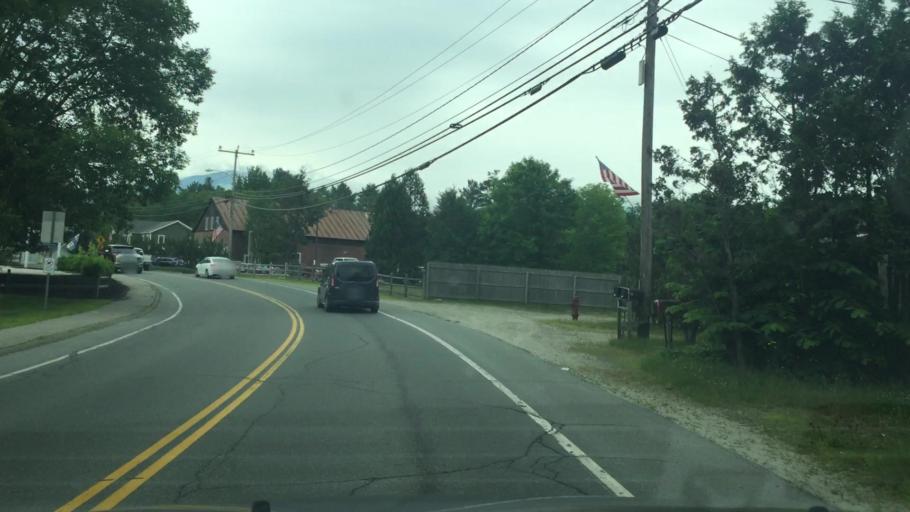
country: US
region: New Hampshire
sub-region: Grafton County
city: Littleton
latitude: 44.2296
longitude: -71.7538
